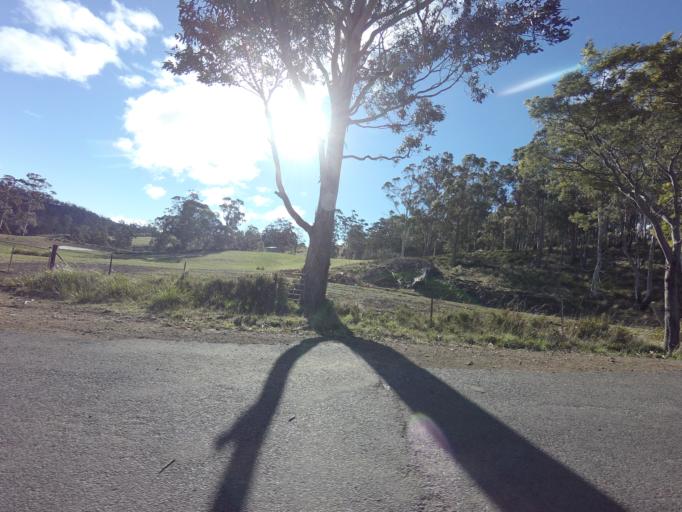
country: AU
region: Tasmania
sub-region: Derwent Valley
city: New Norfolk
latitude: -42.7205
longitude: 147.0328
